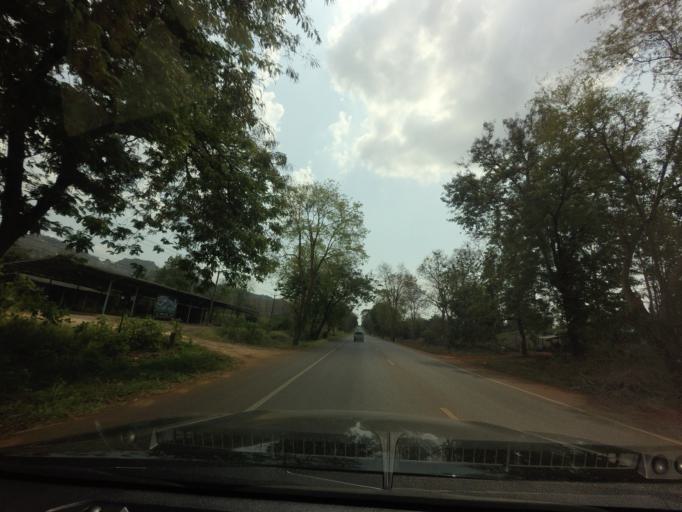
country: TH
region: Kanchanaburi
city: Sai Yok
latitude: 14.1603
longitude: 99.1372
